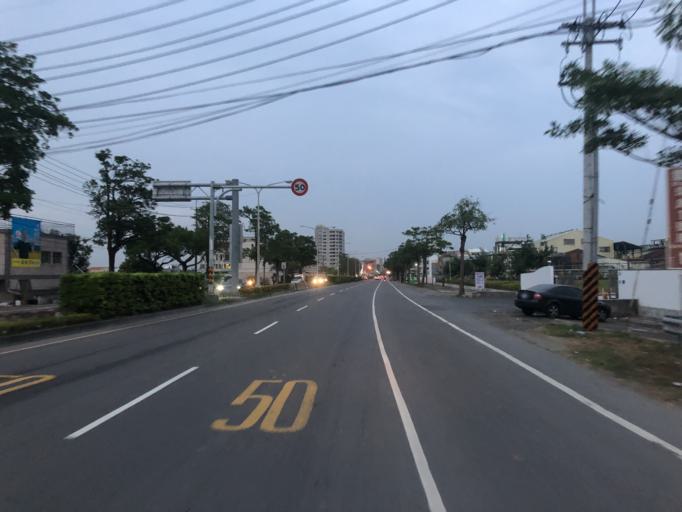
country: TW
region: Taiwan
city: Yujing
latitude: 23.1192
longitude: 120.3185
